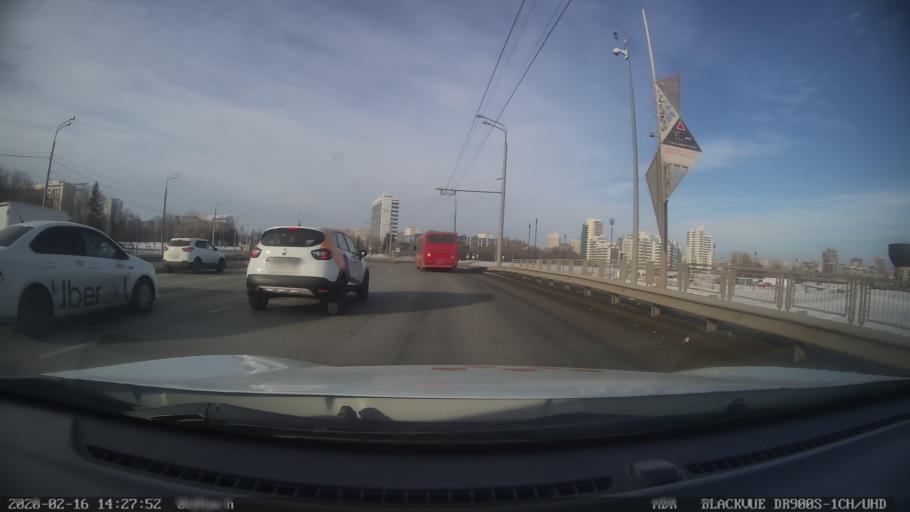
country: RU
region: Tatarstan
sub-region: Gorod Kazan'
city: Kazan
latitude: 55.8108
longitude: 49.1040
